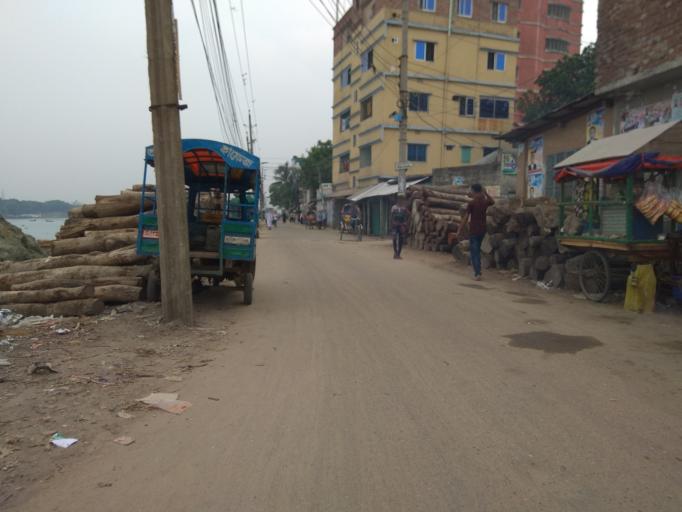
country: BD
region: Dhaka
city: Azimpur
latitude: 23.7126
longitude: 90.3627
